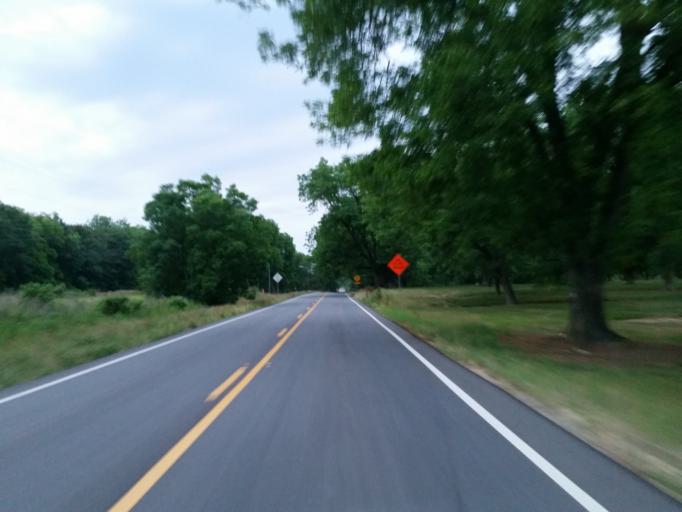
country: US
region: Georgia
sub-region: Turner County
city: Ashburn
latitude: 31.7825
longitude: -83.6987
